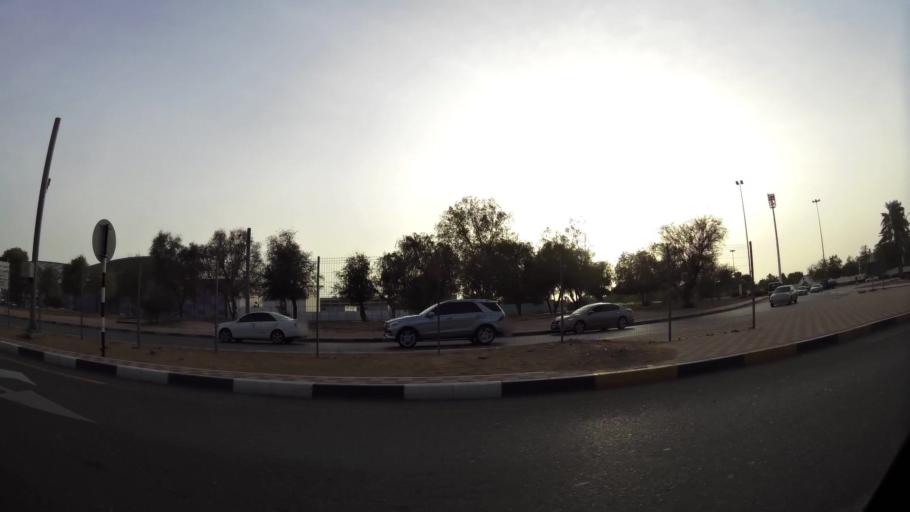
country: AE
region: Abu Dhabi
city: Al Ain
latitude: 24.2473
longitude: 55.7197
